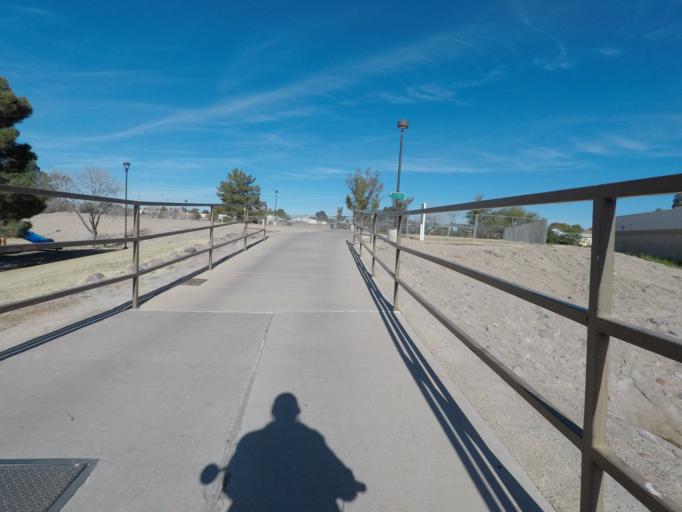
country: US
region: Arizona
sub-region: Maricopa County
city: Tempe
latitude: 33.4544
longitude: -111.9123
